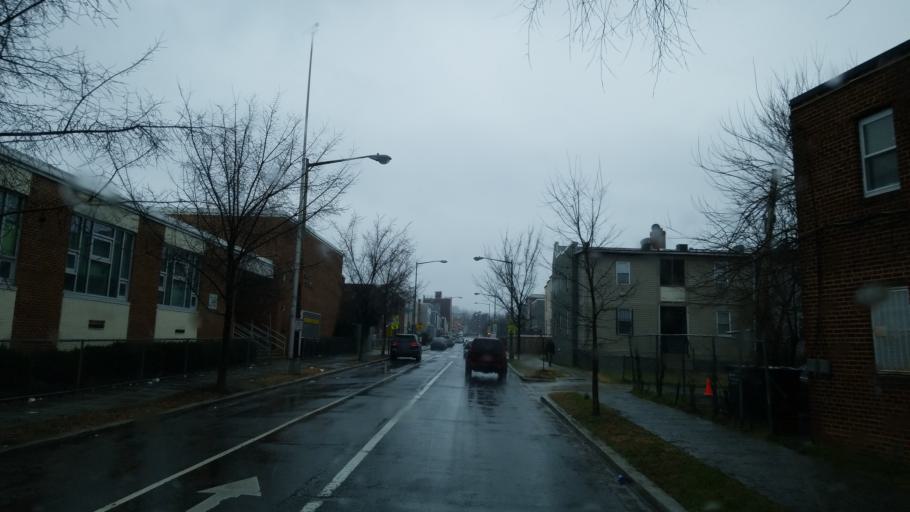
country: US
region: Maryland
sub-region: Prince George's County
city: Mount Rainier
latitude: 38.8962
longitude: -76.9772
